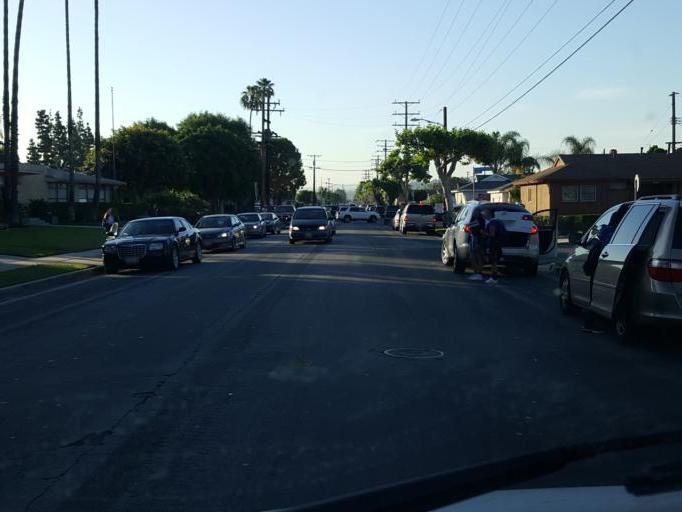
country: US
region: California
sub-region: Los Angeles County
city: West Puente Valley
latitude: 34.0542
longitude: -117.9659
